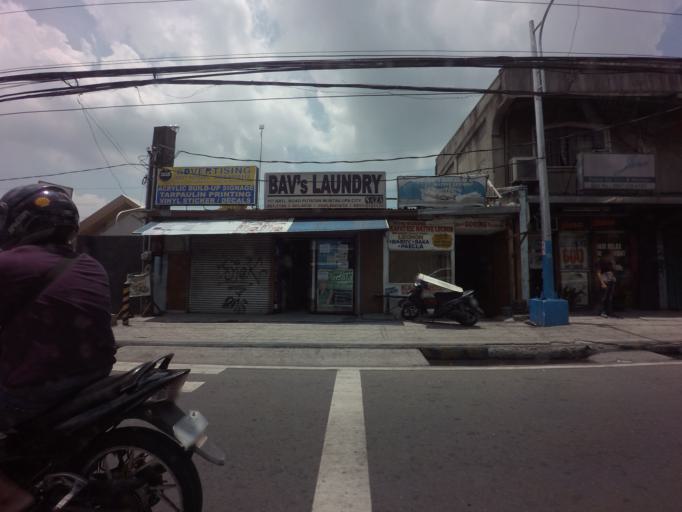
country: PH
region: Calabarzon
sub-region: Province of Laguna
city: San Pedro
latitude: 14.4048
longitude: 121.0470
